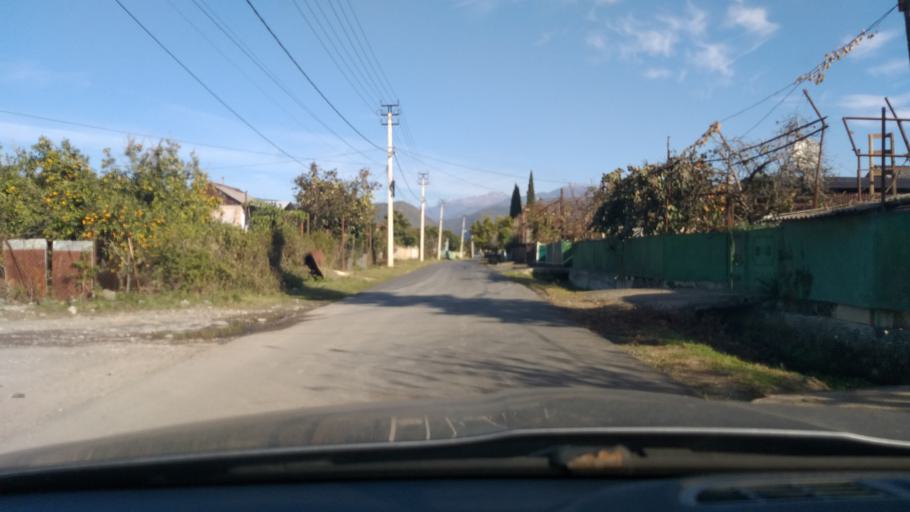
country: GE
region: Abkhazia
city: Sokhumi
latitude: 43.0173
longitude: 40.9655
